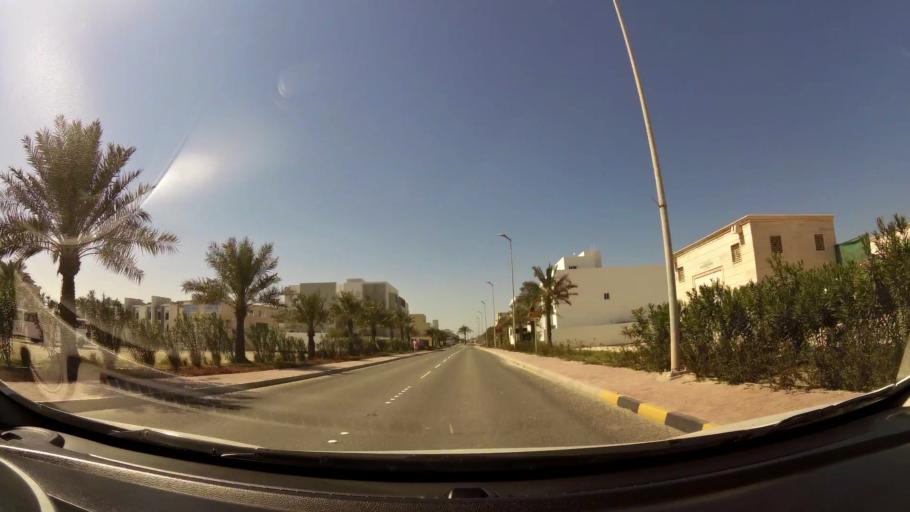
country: BH
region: Muharraq
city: Al Hadd
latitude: 26.2972
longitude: 50.6700
